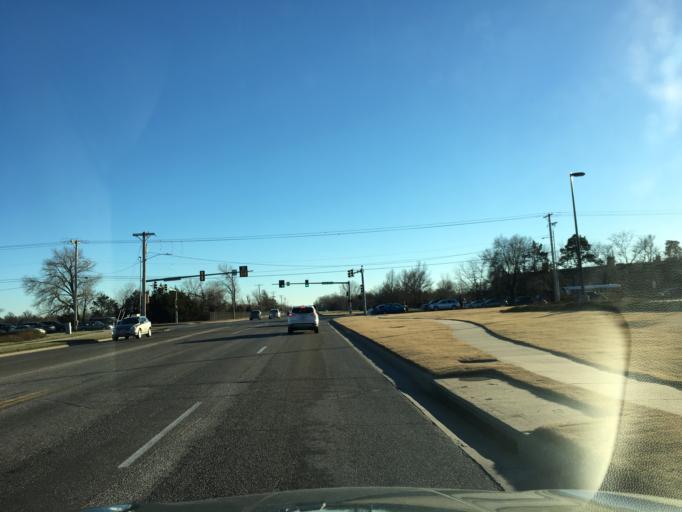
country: US
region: Kansas
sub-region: Sedgwick County
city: Bellaire
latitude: 37.7093
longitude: -97.2263
